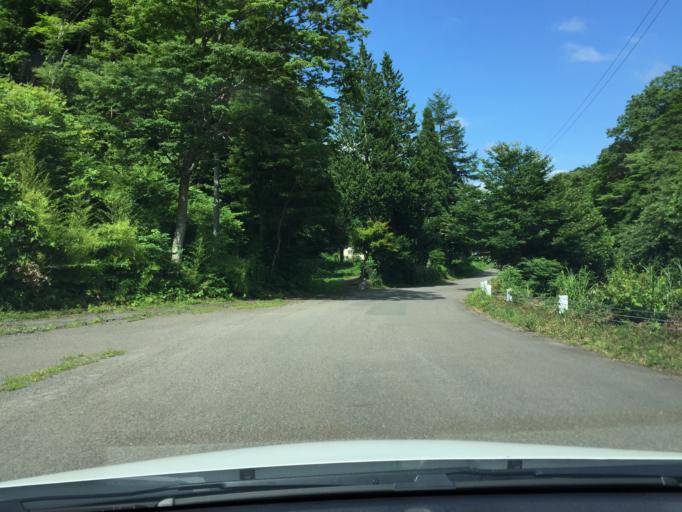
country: JP
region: Fukushima
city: Inawashiro
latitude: 37.2958
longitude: 140.0682
